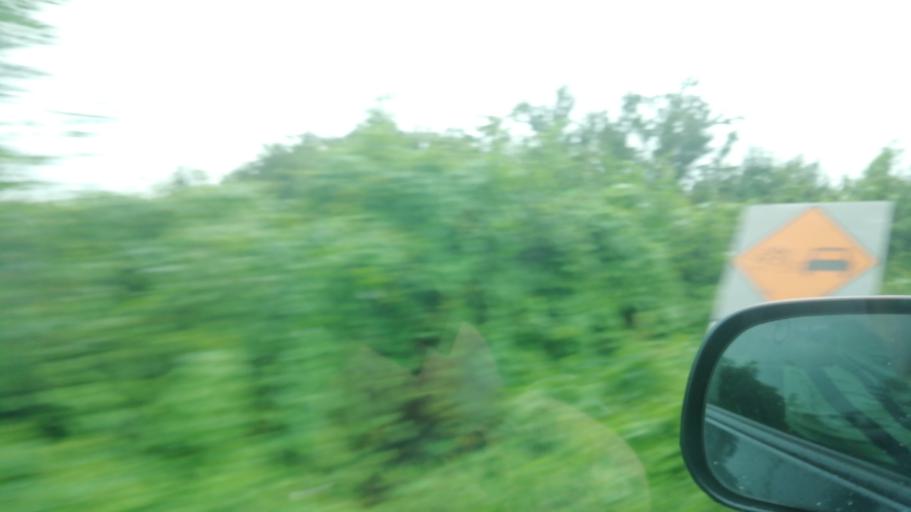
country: IE
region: Leinster
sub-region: Kilkenny
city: Thomastown
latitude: 52.6031
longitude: -7.1425
